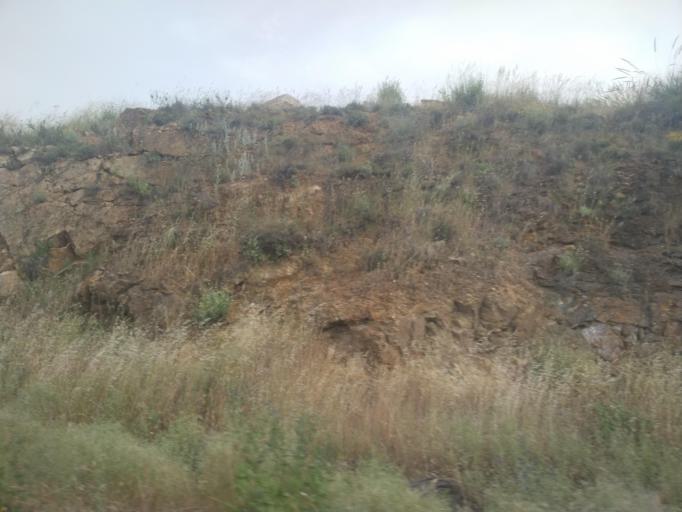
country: ES
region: Castille-La Mancha
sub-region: Province of Toledo
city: Guadamur
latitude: 39.8102
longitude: -4.1174
